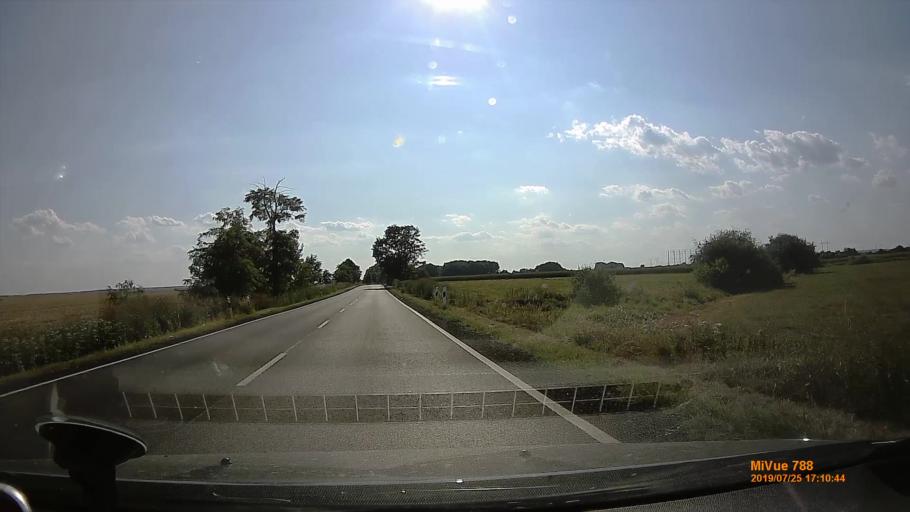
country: HU
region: Pest
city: Galgaheviz
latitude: 47.6508
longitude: 19.5704
